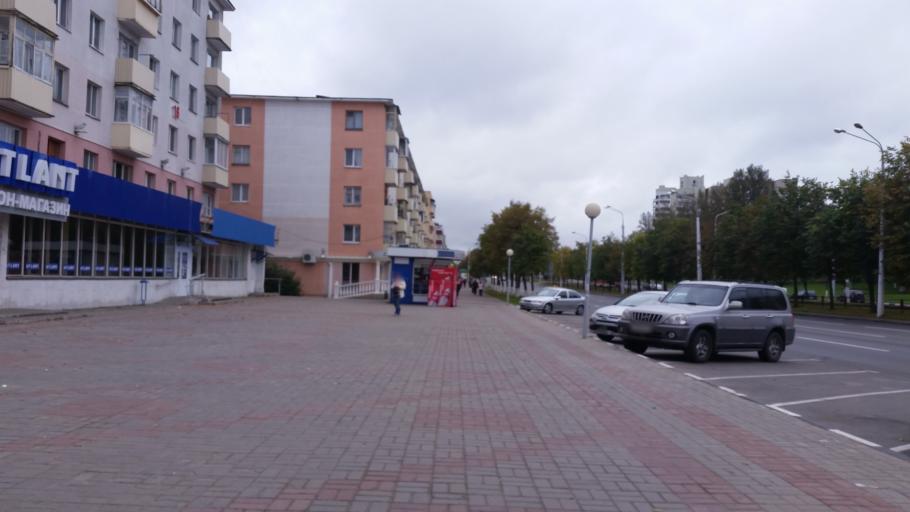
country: BY
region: Vitebsk
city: Vitebsk
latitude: 55.1817
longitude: 30.2105
